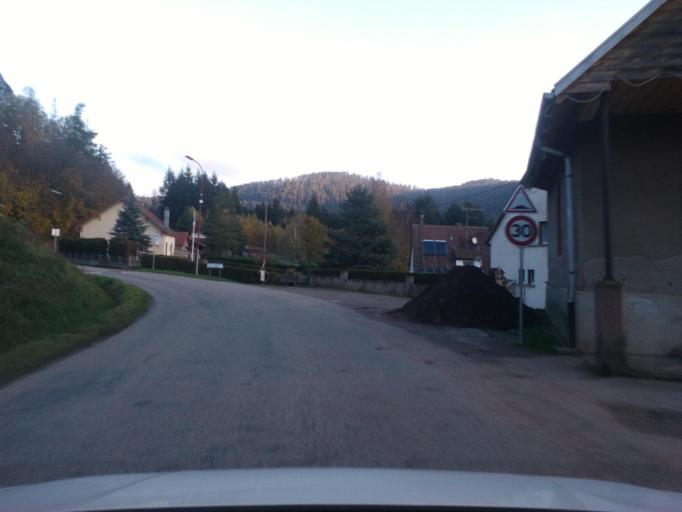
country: FR
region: Lorraine
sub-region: Departement des Vosges
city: Ban-de-Laveline
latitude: 48.3531
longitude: 7.1061
